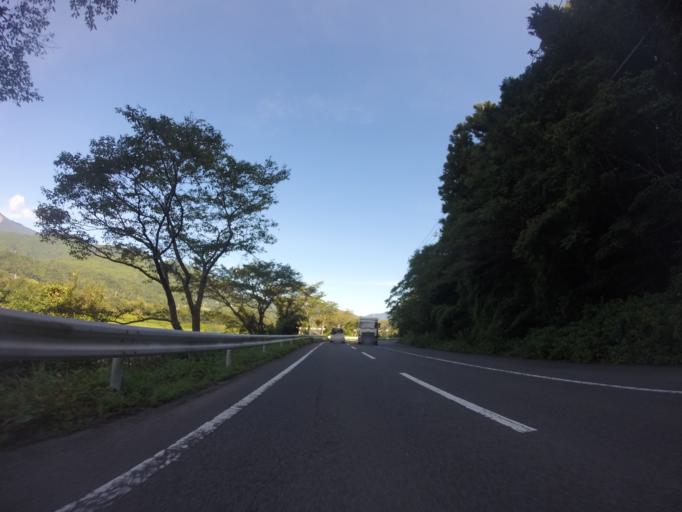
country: JP
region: Shizuoka
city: Fujinomiya
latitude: 35.3023
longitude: 138.4571
